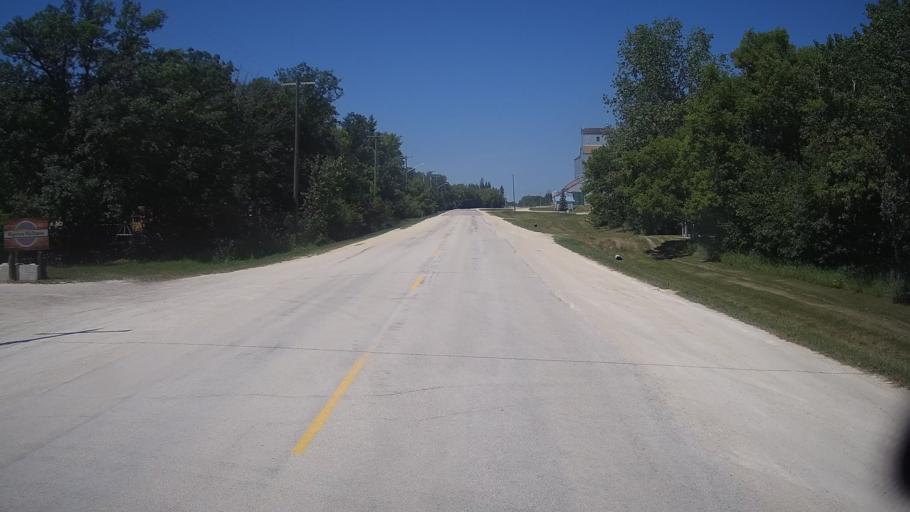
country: CA
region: Manitoba
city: Stonewall
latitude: 50.1316
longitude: -97.5466
